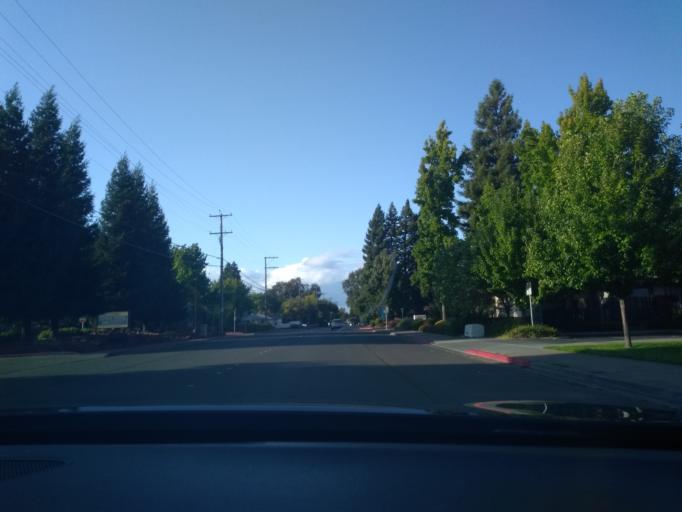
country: US
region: California
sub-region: Mendocino County
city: Ukiah
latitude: 39.1473
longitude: -123.1988
